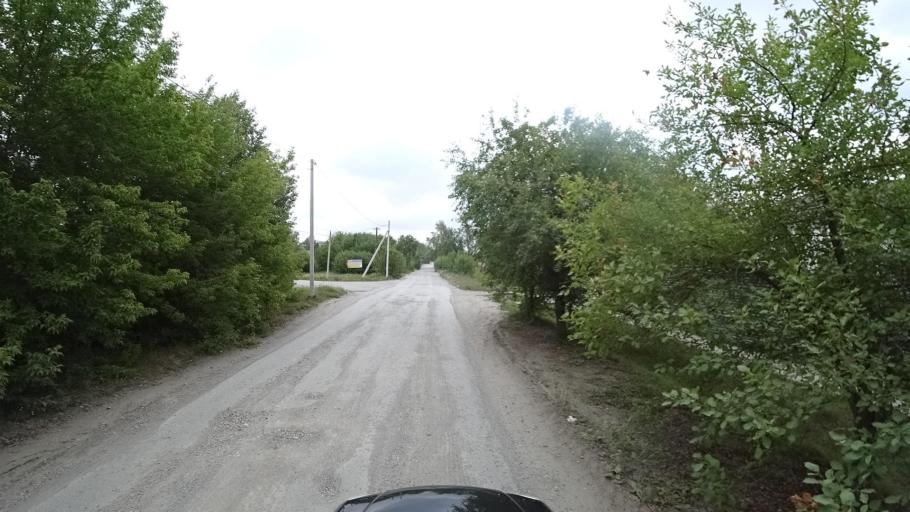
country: RU
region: Sverdlovsk
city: Kamyshlov
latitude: 56.8333
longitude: 62.7202
